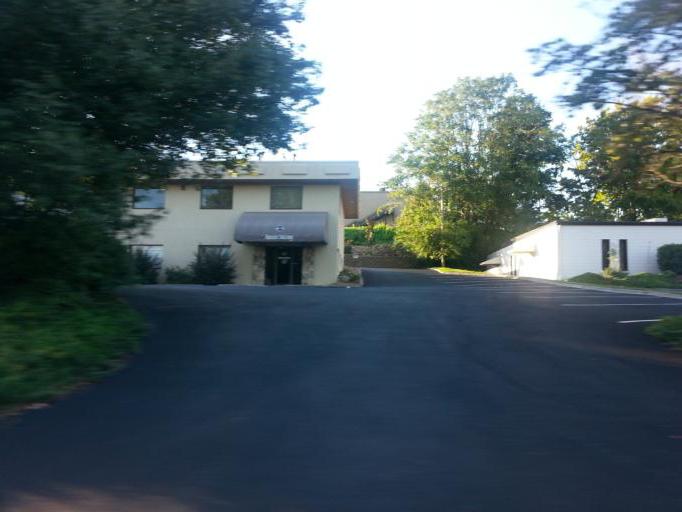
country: US
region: Tennessee
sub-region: Knox County
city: Knoxville
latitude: 35.9305
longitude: -84.0089
